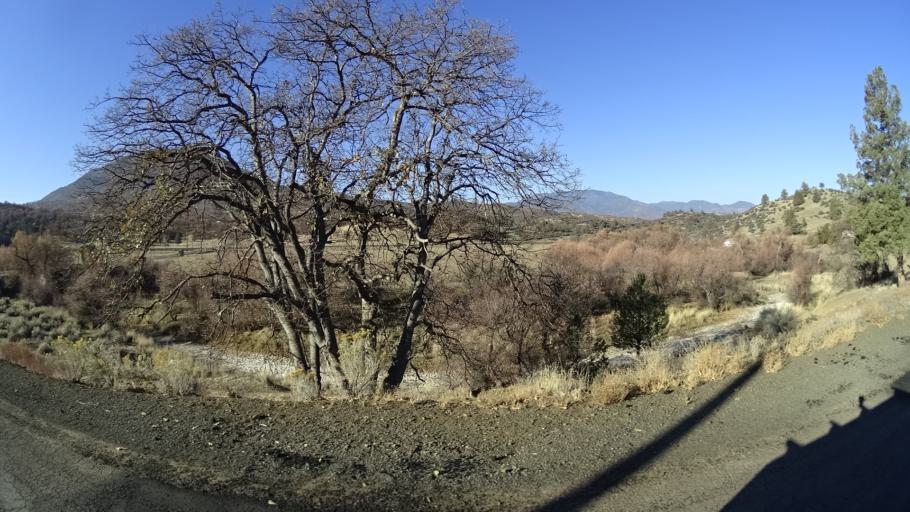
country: US
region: California
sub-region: Siskiyou County
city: Montague
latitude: 41.8912
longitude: -122.4812
